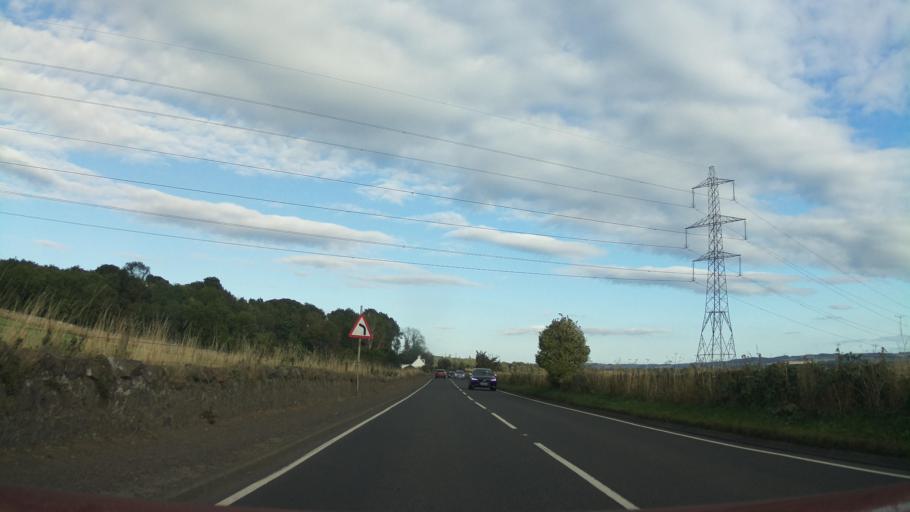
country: GB
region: Scotland
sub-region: Fife
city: Auchtermuchty
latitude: 56.2933
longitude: -3.2190
